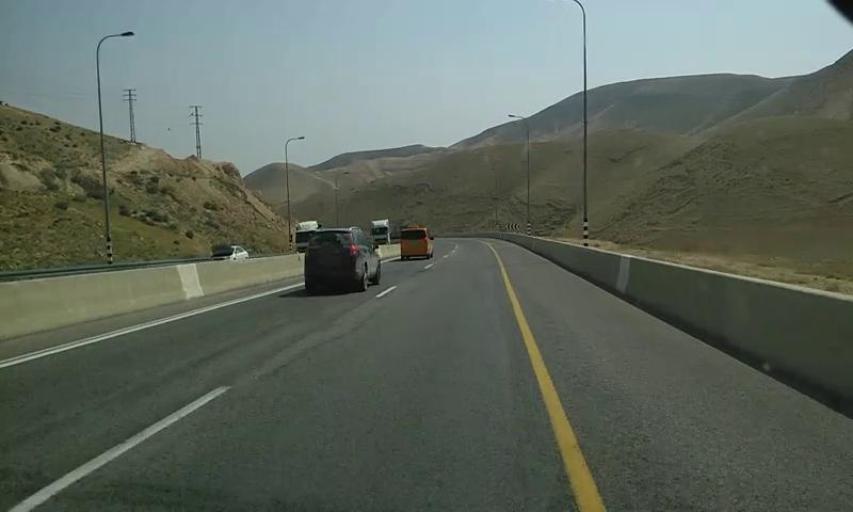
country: PS
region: West Bank
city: Jericho
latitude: 31.8113
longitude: 35.3904
